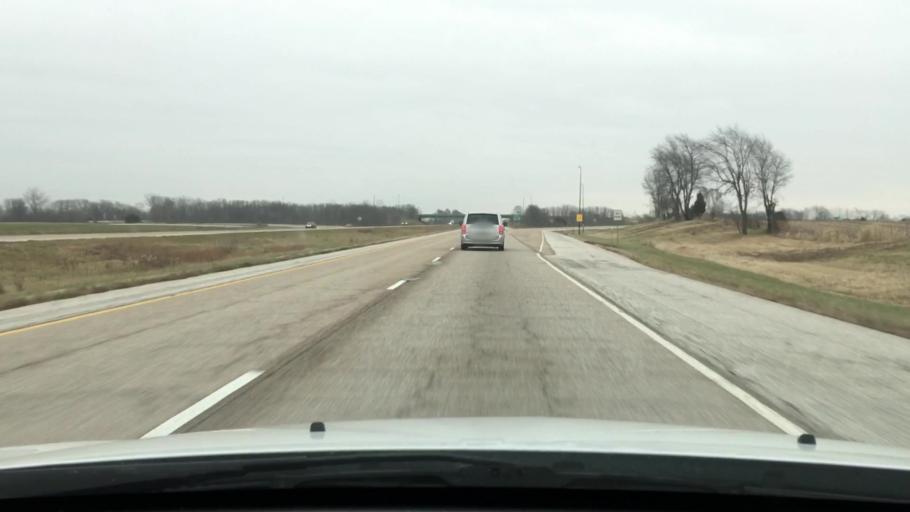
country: US
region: Illinois
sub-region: Scott County
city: Winchester
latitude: 39.6809
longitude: -90.4638
